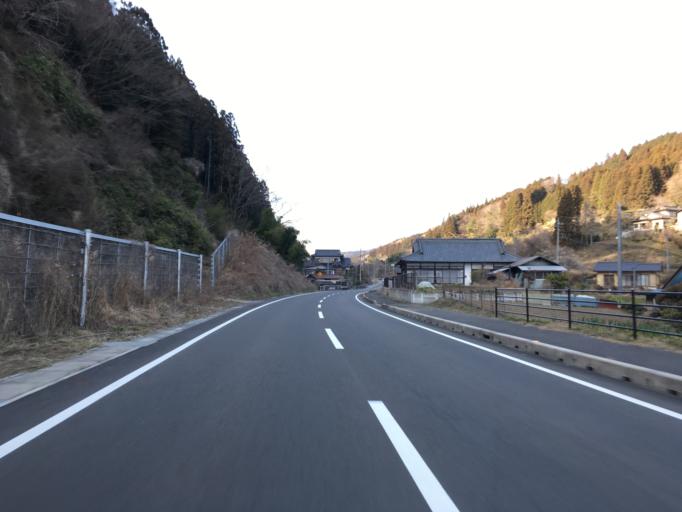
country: JP
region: Ibaraki
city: Daigo
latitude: 36.7143
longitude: 140.4633
